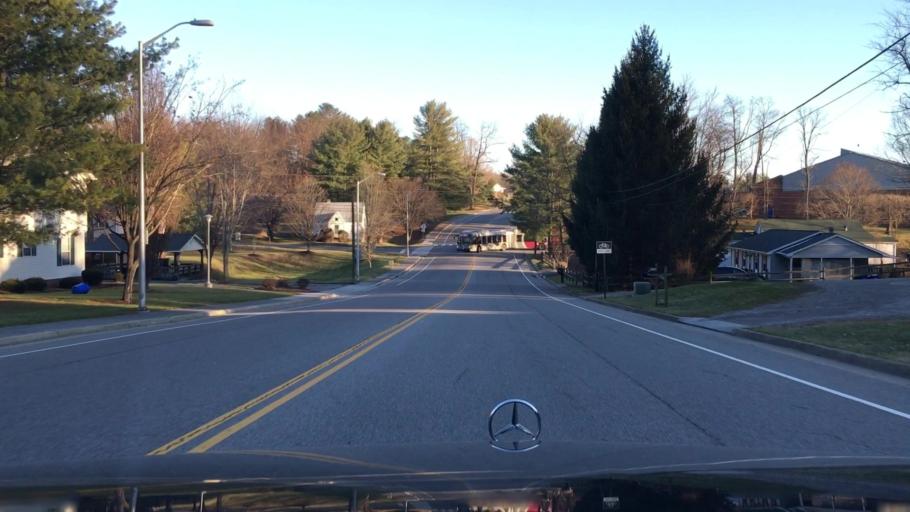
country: US
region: Virginia
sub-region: Montgomery County
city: Blacksburg
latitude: 37.2456
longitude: -80.4135
